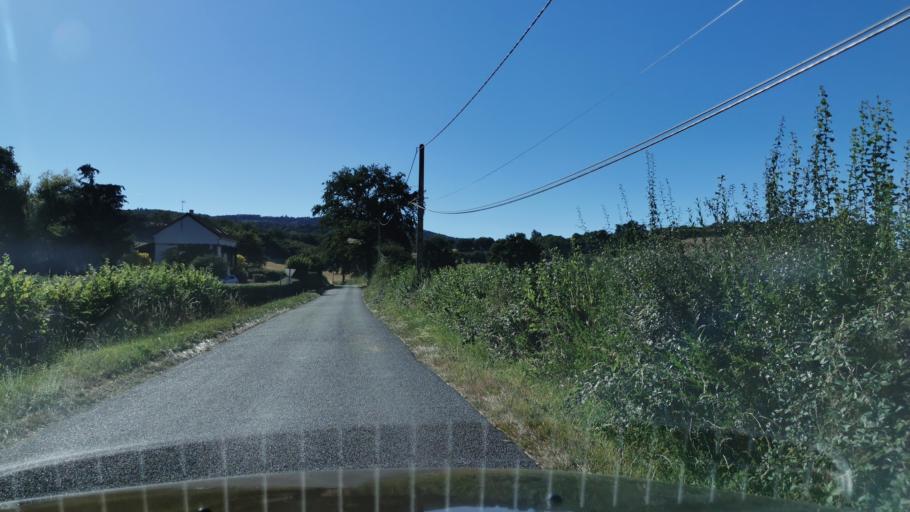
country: FR
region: Bourgogne
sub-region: Departement de Saone-et-Loire
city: Marmagne
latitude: 46.8044
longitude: 4.3282
